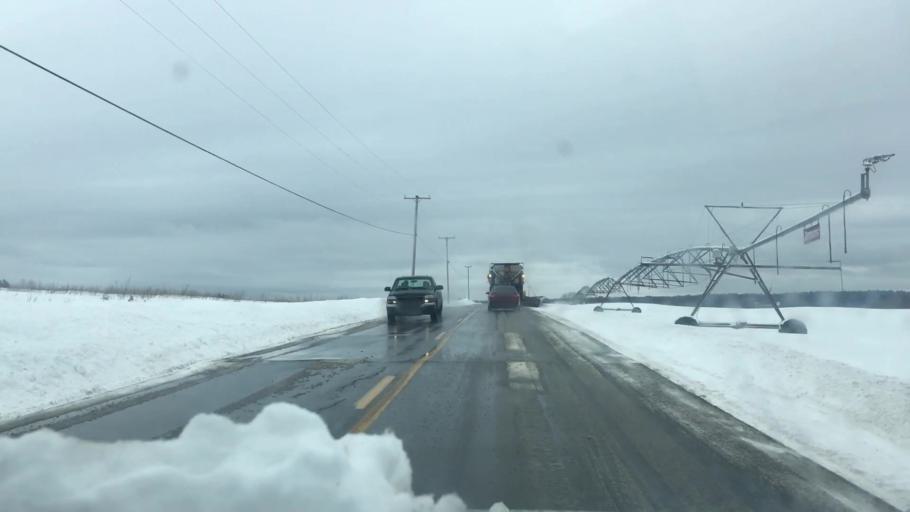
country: US
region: Maine
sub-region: Penobscot County
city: Garland
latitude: 44.9786
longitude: -69.1045
